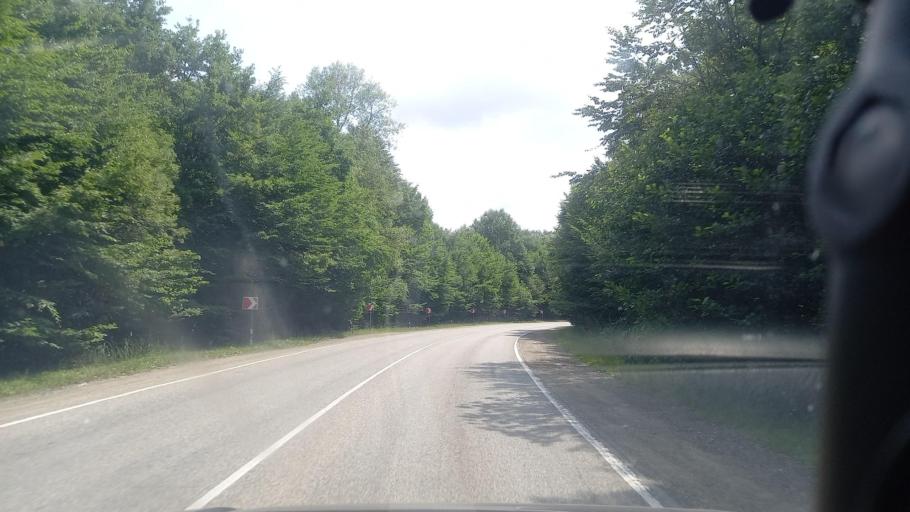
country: RU
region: Karachayevo-Cherkesiya
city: Kurdzhinovo
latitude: 44.0389
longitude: 40.9026
